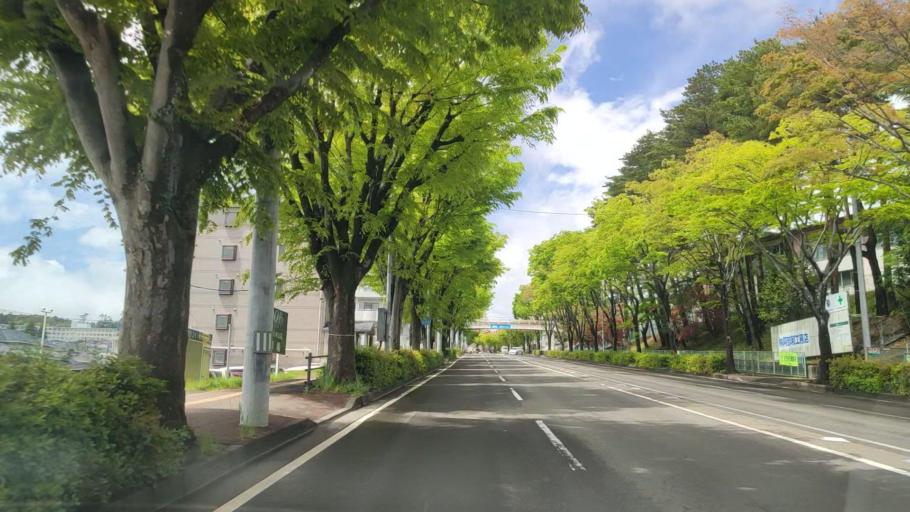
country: JP
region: Miyagi
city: Sendai
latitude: 38.2385
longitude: 140.8485
